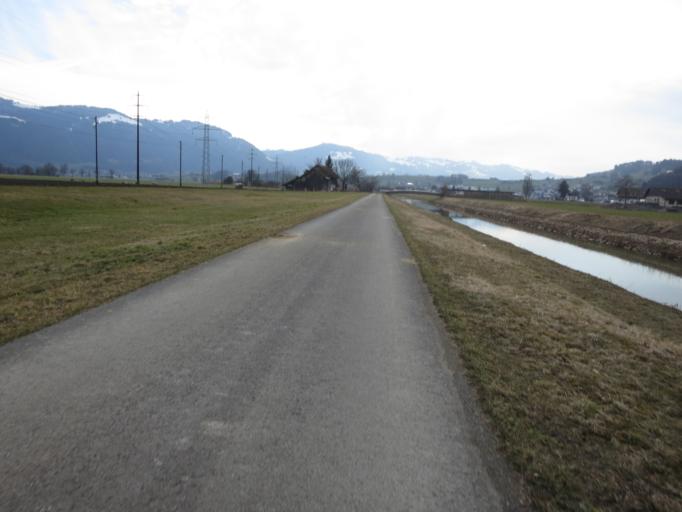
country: CH
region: Schwyz
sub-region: Bezirk March
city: Tuggen
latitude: 47.2082
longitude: 8.9617
